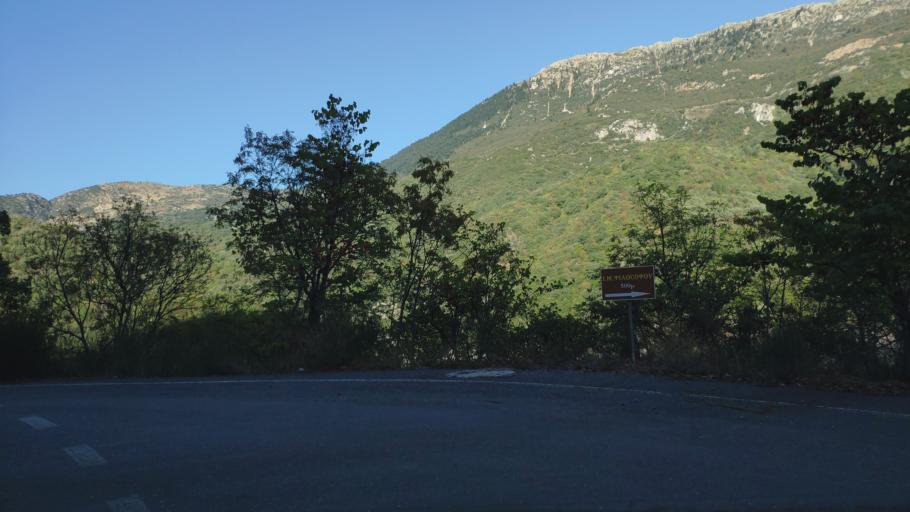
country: GR
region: Peloponnese
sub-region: Nomos Arkadias
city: Dimitsana
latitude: 37.5593
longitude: 22.0433
